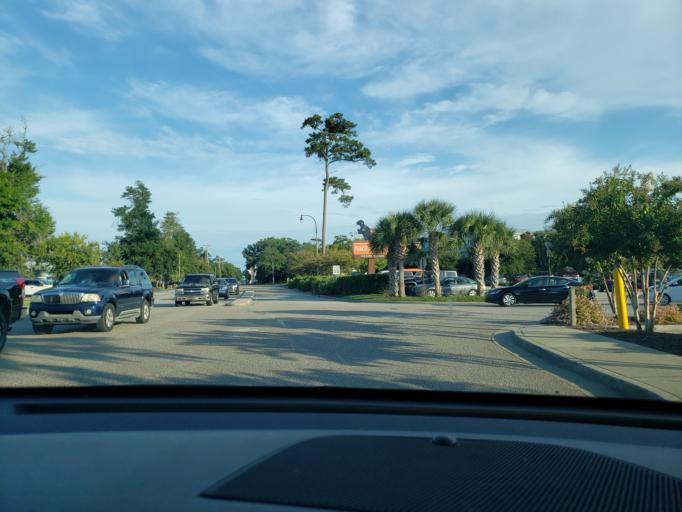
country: US
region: South Carolina
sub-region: Horry County
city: North Myrtle Beach
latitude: 33.7975
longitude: -78.7418
